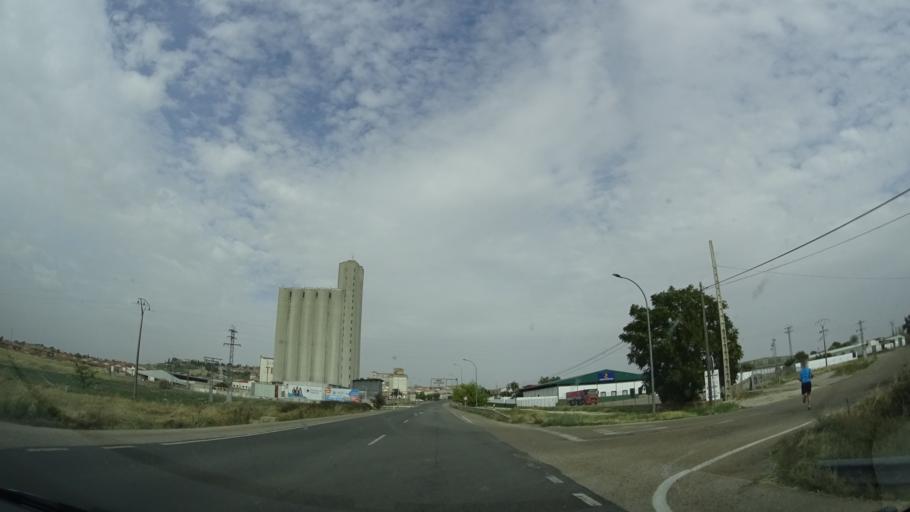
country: ES
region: Extremadura
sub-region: Provincia de Caceres
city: Trujillo
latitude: 39.4498
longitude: -5.8811
